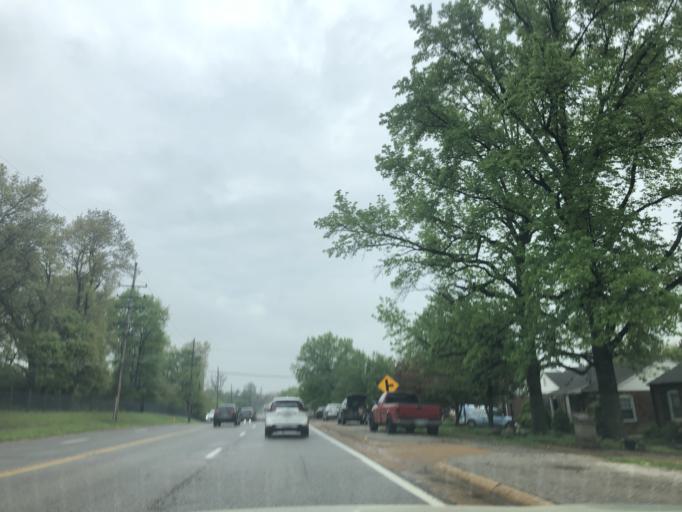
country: US
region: Missouri
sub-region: Saint Louis County
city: Marlborough
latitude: 38.5778
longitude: -90.3188
